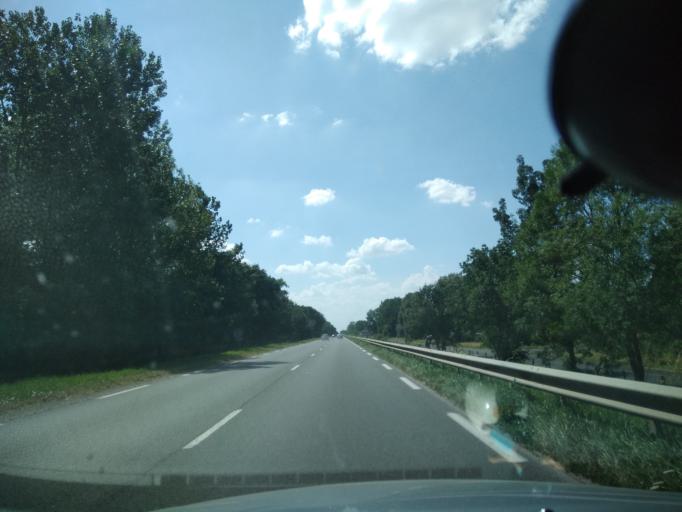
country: FR
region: Centre
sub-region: Departement d'Indre-et-Loire
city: La Ville-aux-Dames
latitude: 47.3812
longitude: 0.7713
